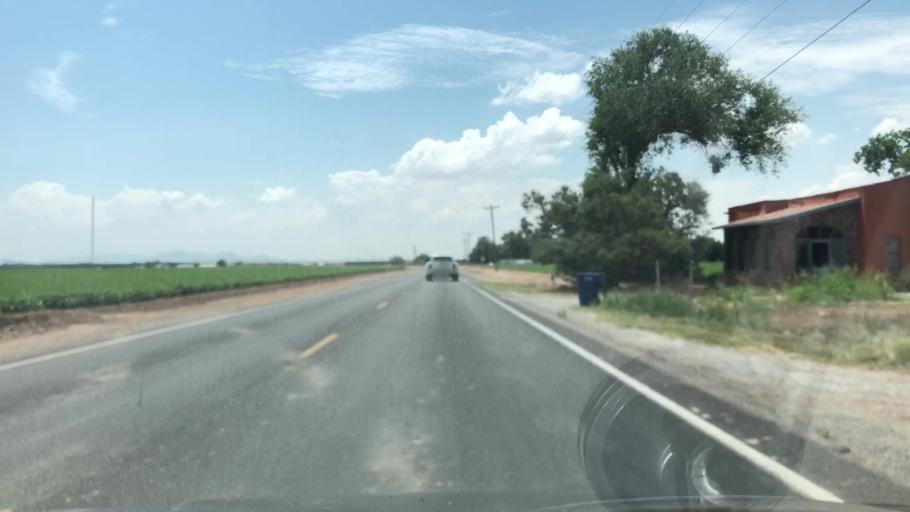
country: US
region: New Mexico
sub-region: Dona Ana County
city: La Union
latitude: 31.9774
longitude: -106.6515
